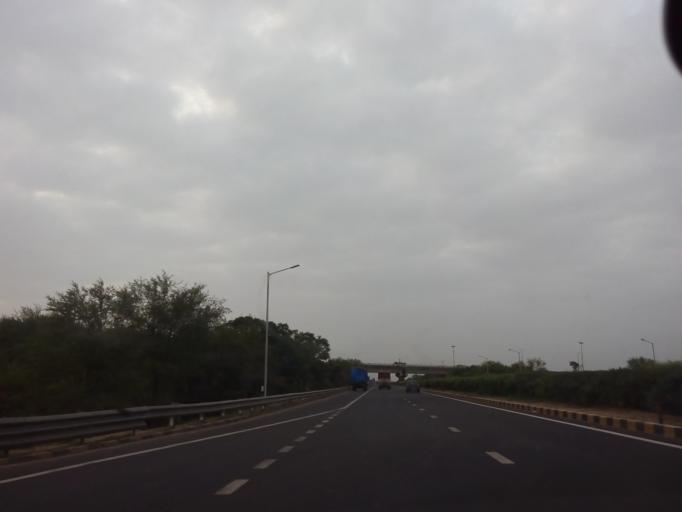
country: IN
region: Gujarat
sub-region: Ahmadabad
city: Ahmedabad
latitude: 22.9711
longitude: 72.6587
